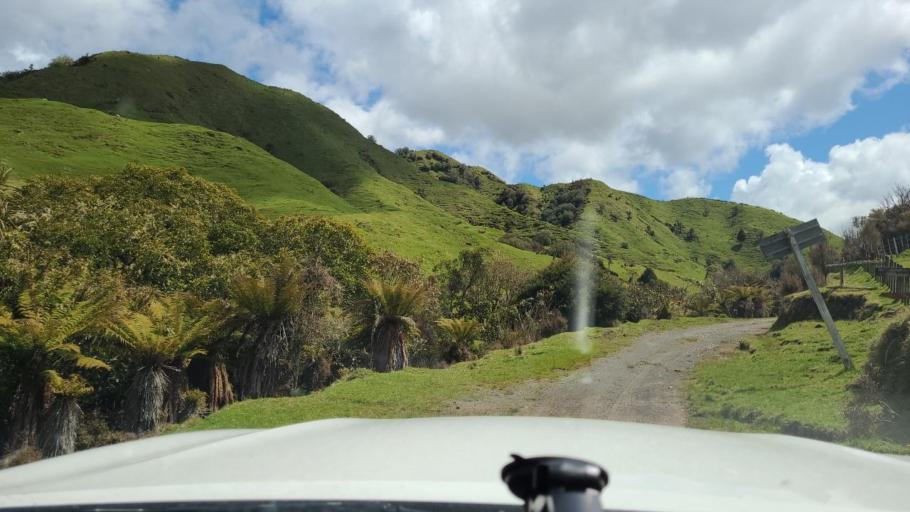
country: NZ
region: Bay of Plenty
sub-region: Opotiki District
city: Opotiki
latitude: -38.2125
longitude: 177.5900
